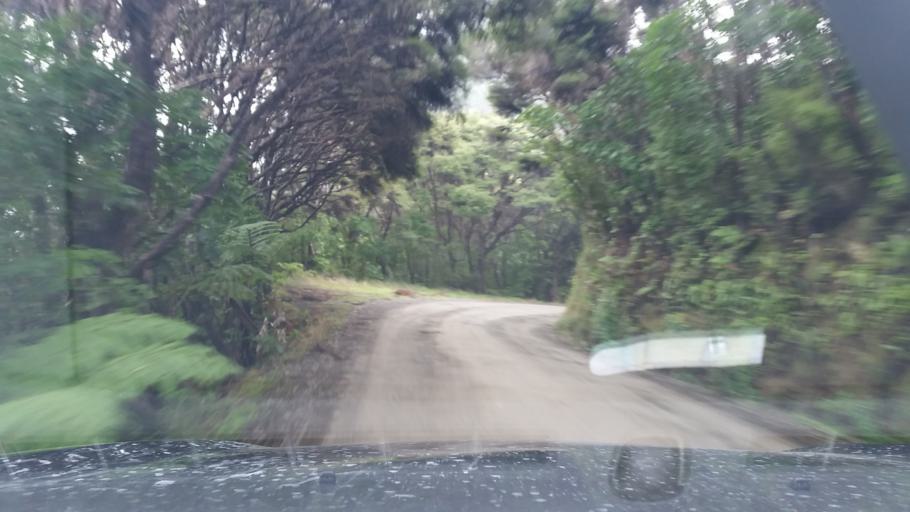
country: NZ
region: Marlborough
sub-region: Marlborough District
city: Picton
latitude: -41.1686
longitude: 174.0197
